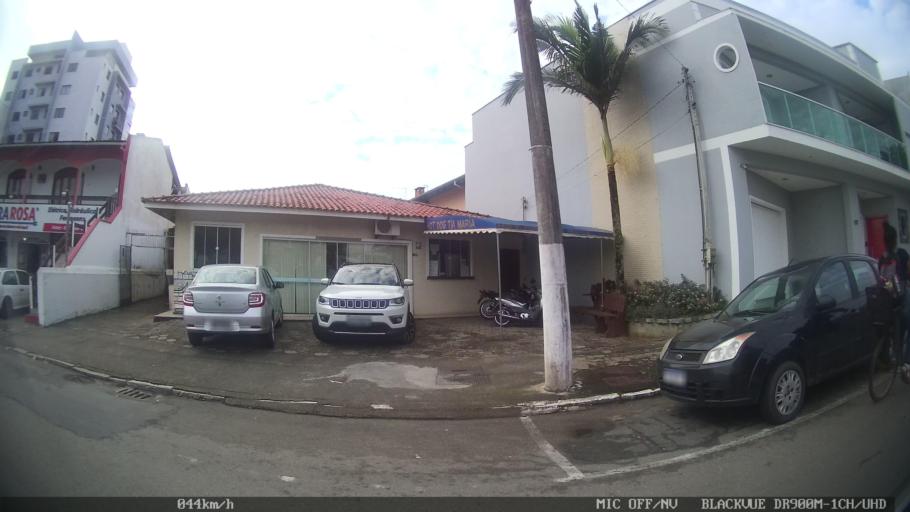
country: BR
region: Santa Catarina
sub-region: Barra Velha
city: Barra Velha
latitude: -26.6409
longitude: -48.6829
